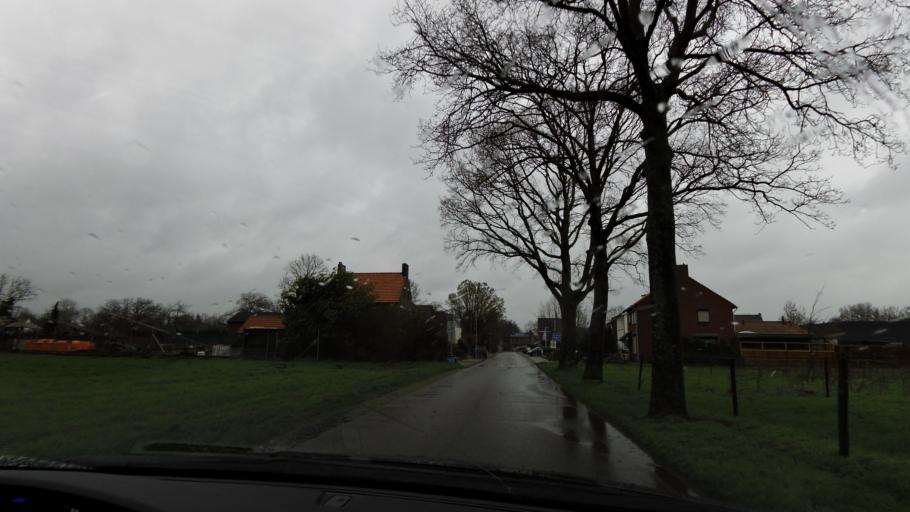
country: NL
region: Limburg
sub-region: Gemeente Sittard-Geleen
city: Born
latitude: 51.0395
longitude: 5.7849
